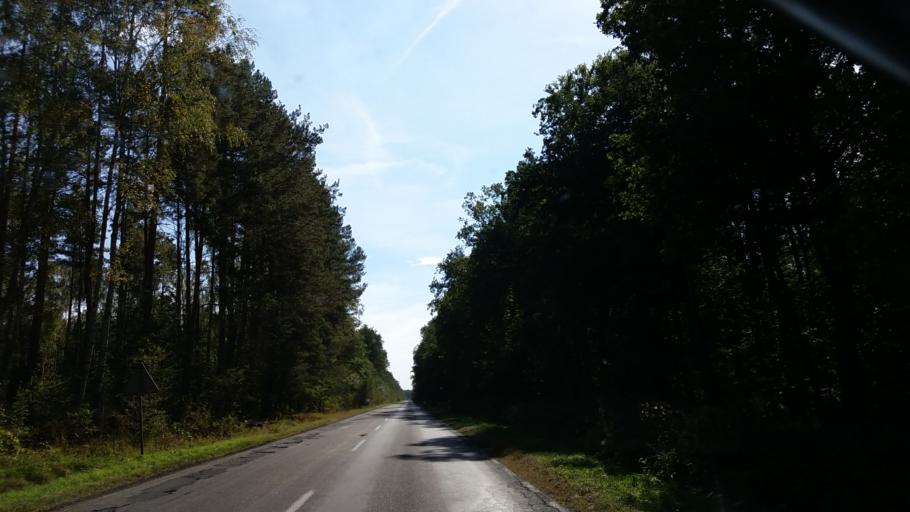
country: PL
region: Lubusz
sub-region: Powiat strzelecko-drezdenecki
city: Drezdenko
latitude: 52.8095
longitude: 15.8290
